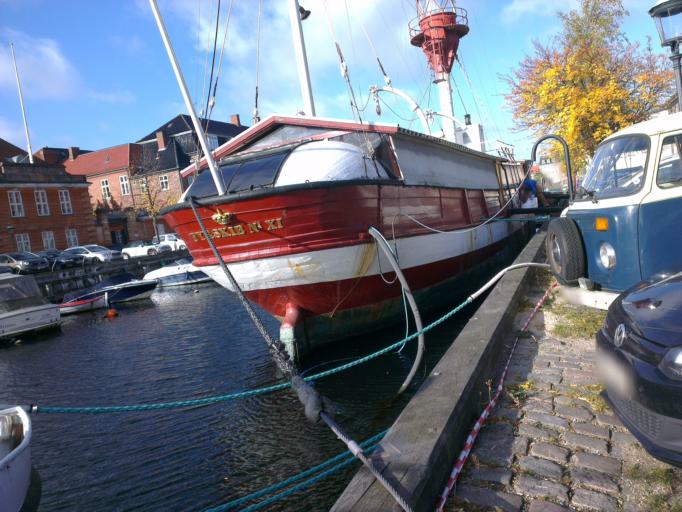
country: DK
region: Capital Region
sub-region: Kobenhavn
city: Copenhagen
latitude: 55.6735
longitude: 12.5787
